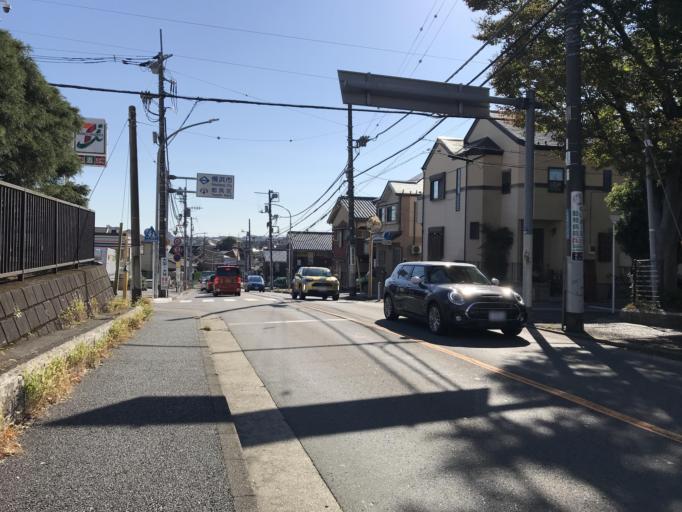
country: JP
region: Tokyo
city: Chofugaoka
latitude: 35.5688
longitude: 139.5841
